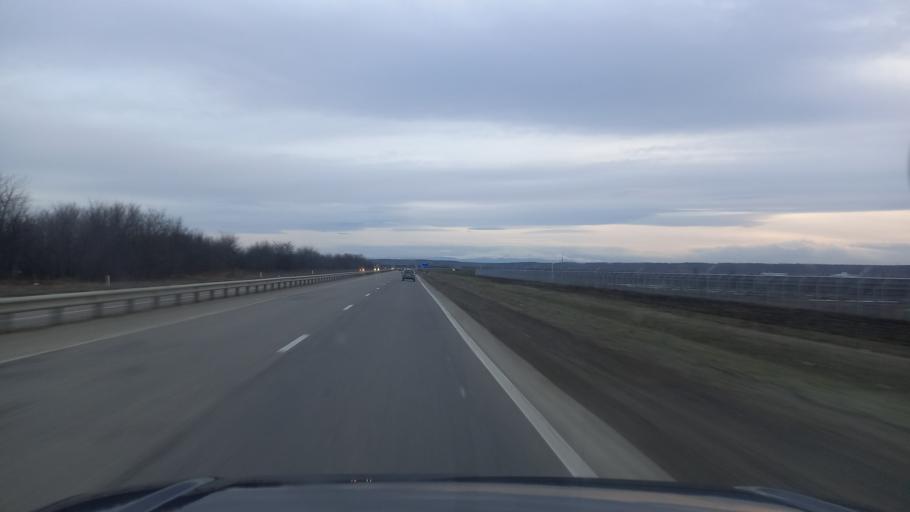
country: RU
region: Adygeya
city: Khanskaya
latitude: 44.6707
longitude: 39.9924
